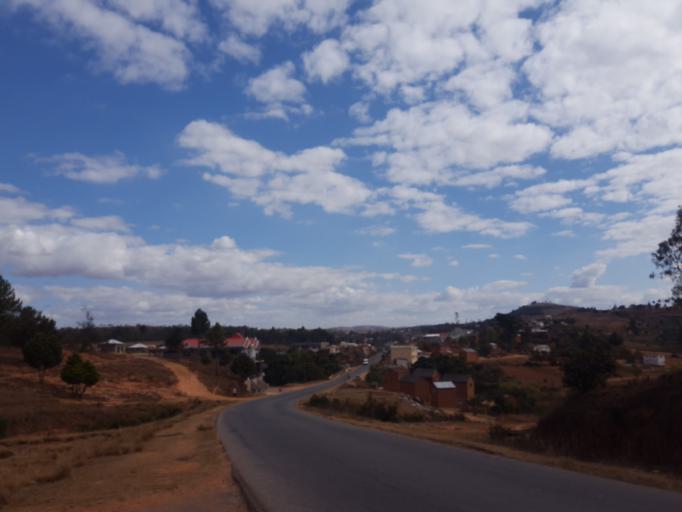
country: MG
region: Analamanga
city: Antananarivo
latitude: -18.9549
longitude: 47.3587
